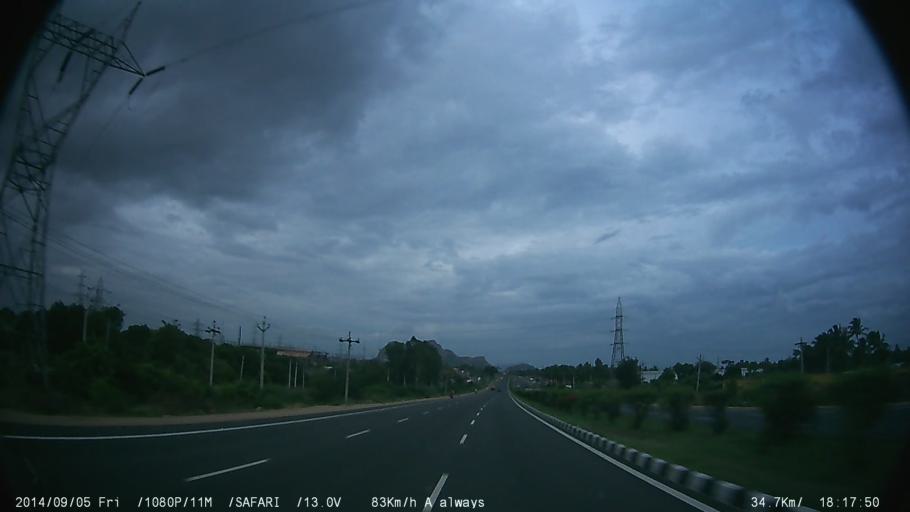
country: IN
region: Tamil Nadu
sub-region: Krishnagiri
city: Kelamangalam
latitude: 12.6702
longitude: 77.9863
